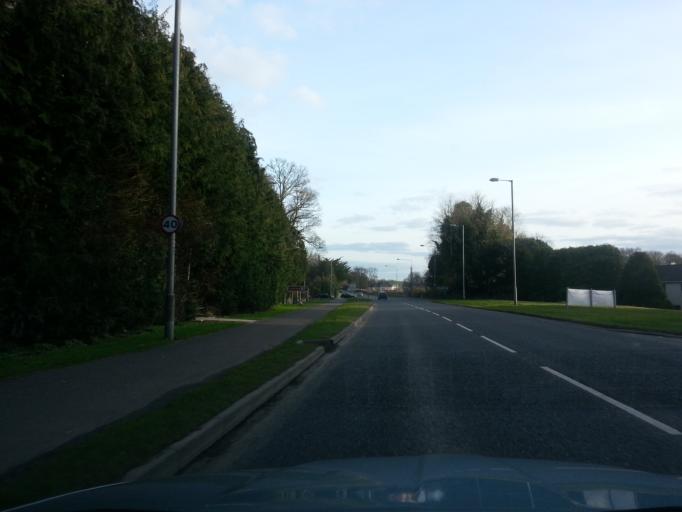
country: GB
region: Northern Ireland
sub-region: Fermanagh District
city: Enniskillen
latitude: 54.3370
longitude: -7.6248
